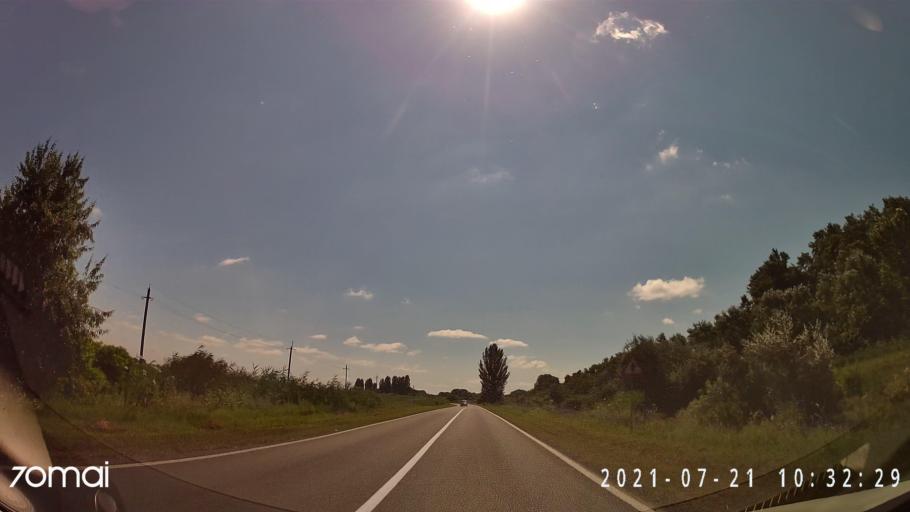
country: RO
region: Tulcea
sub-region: Oras Isaccea
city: Isaccea
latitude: 45.3014
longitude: 28.4247
